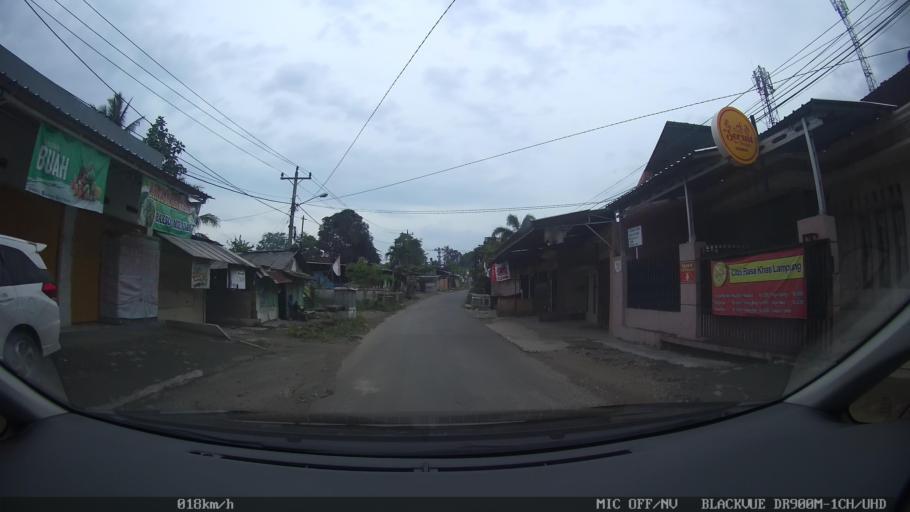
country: ID
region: Lampung
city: Kedaton
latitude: -5.3848
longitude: 105.2493
